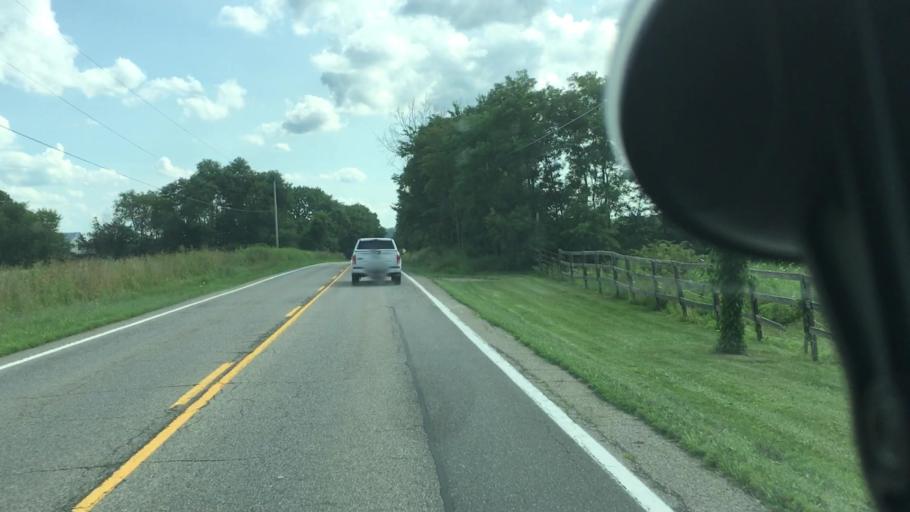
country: US
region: Ohio
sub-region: Columbiana County
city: Salem
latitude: 40.9651
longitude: -80.8299
